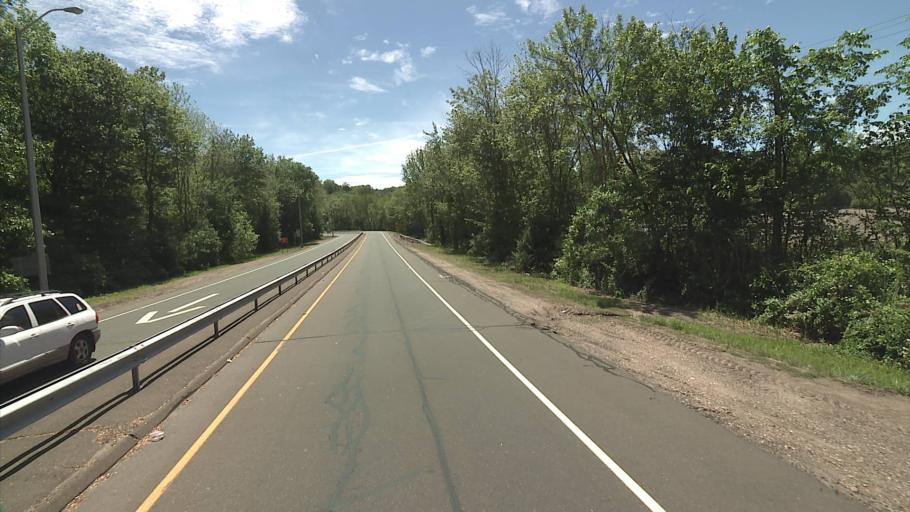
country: US
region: Connecticut
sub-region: New Haven County
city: Branford
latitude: 41.2928
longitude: -72.7830
